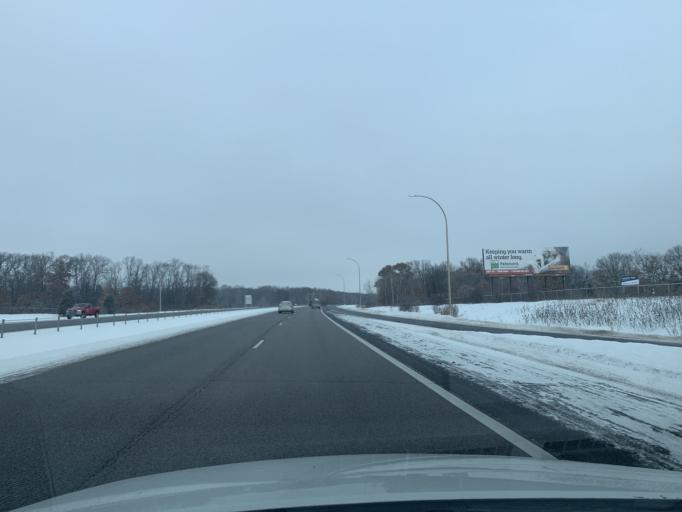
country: US
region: Minnesota
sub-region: Chisago County
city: Stacy
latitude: 45.3988
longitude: -92.9948
